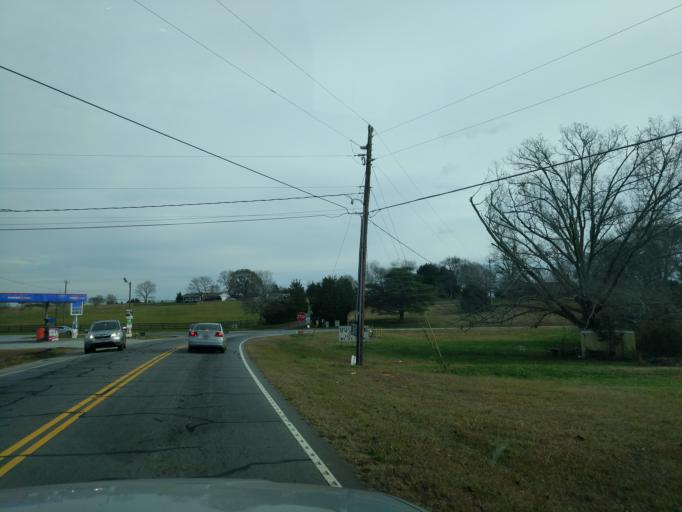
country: US
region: South Carolina
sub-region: Pickens County
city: Central
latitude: 34.6950
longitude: -82.7474
